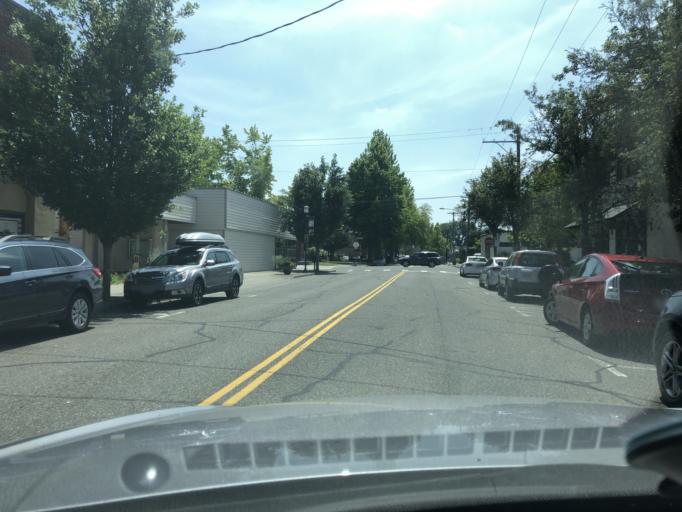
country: US
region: Washington
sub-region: King County
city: Kent
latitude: 47.3815
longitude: -122.2349
